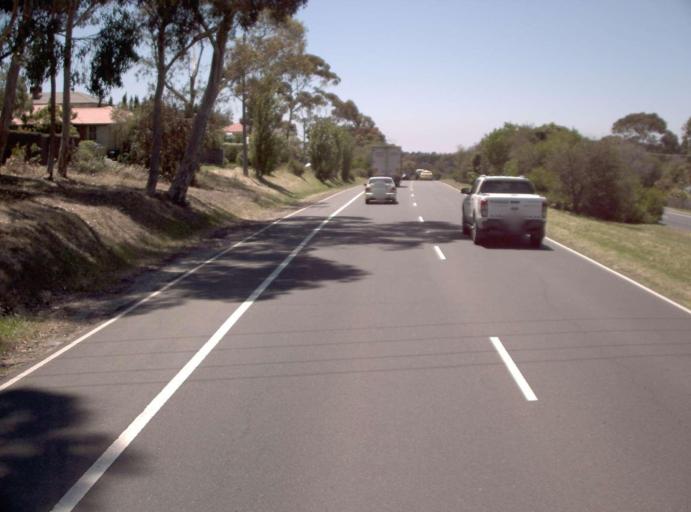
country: AU
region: Victoria
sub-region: Mornington Peninsula
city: Mount Eliza
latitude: -38.1887
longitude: 145.0954
